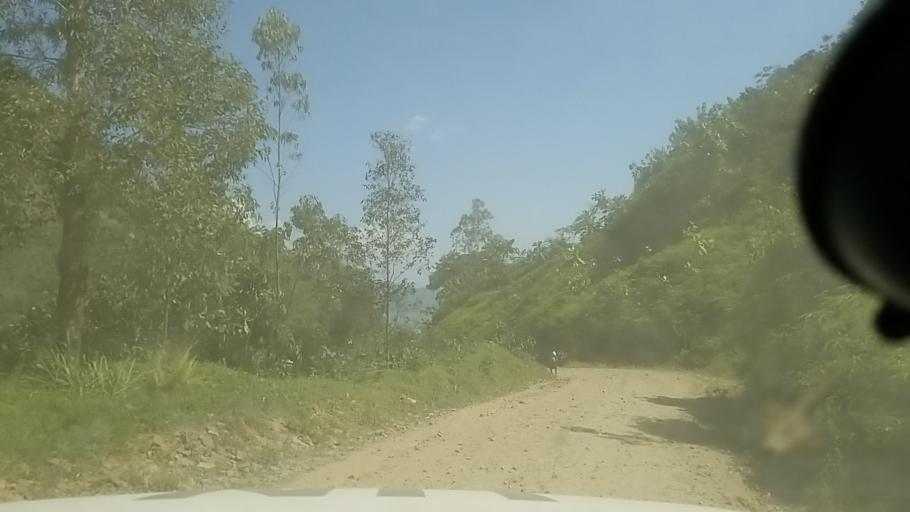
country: CD
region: Nord Kivu
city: Sake
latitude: -1.9665
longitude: 28.9150
